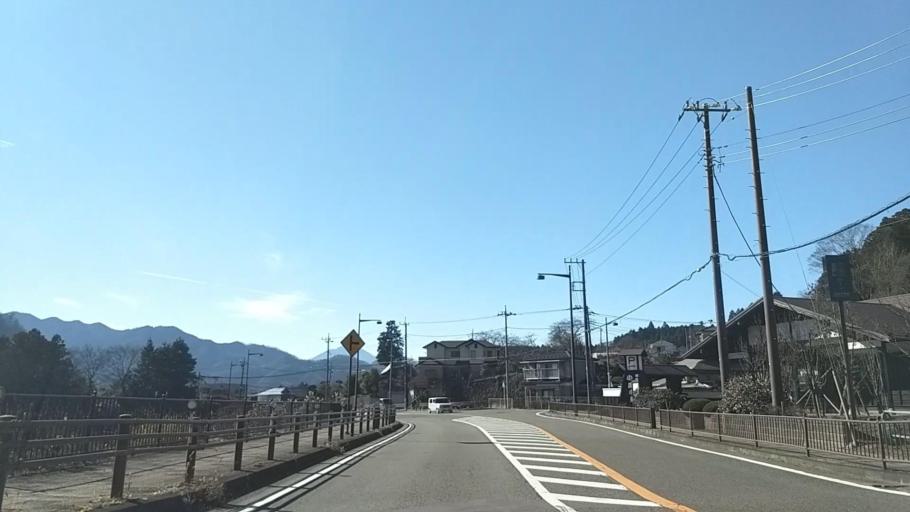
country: JP
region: Yamanashi
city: Uenohara
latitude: 35.6228
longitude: 139.2017
